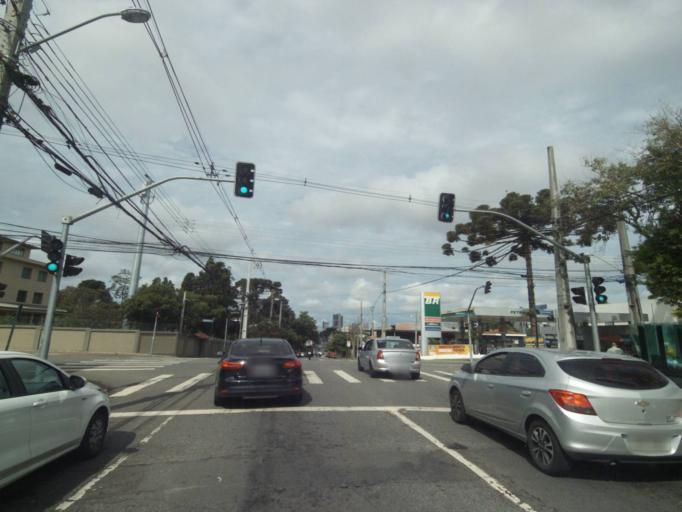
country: BR
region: Parana
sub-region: Curitiba
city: Curitiba
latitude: -25.4416
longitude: -49.2982
